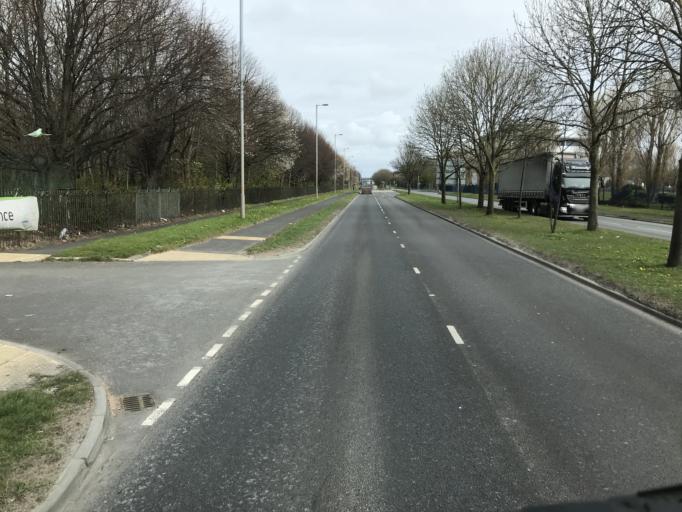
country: GB
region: England
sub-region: Sefton
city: Litherland
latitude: 53.4778
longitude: -2.9769
